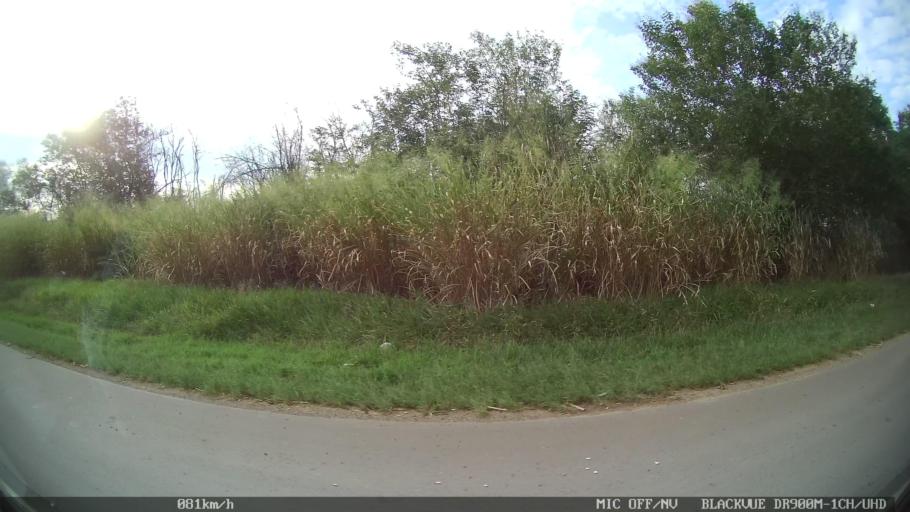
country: BR
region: Sao Paulo
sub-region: Cosmopolis
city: Cosmopolis
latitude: -22.6121
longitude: -47.2323
